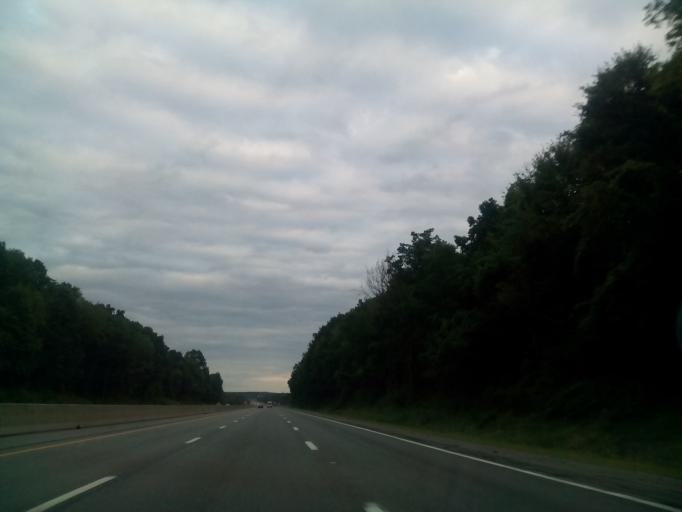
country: US
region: Ohio
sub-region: Portage County
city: Windham
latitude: 41.2432
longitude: -81.0774
